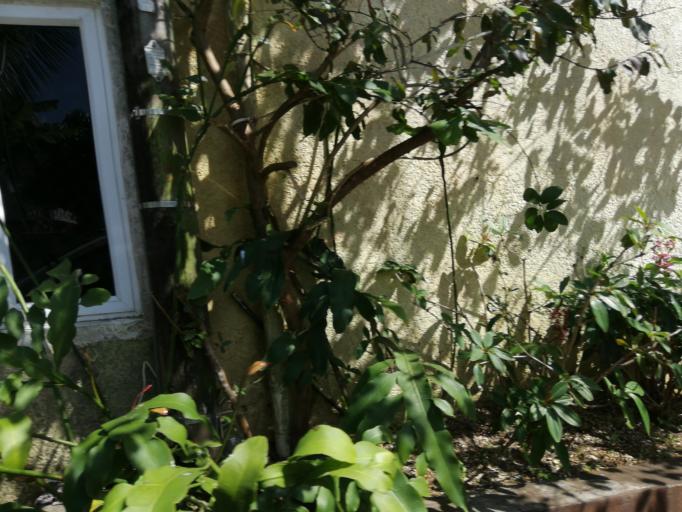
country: MU
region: Moka
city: Moka
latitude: -20.2168
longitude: 57.4917
